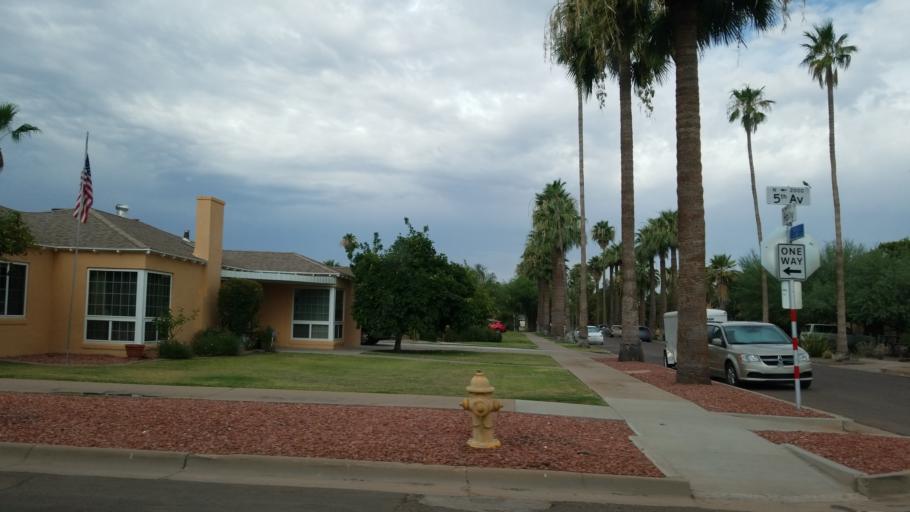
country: US
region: Arizona
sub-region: Maricopa County
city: Phoenix
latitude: 33.4702
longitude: -112.0803
